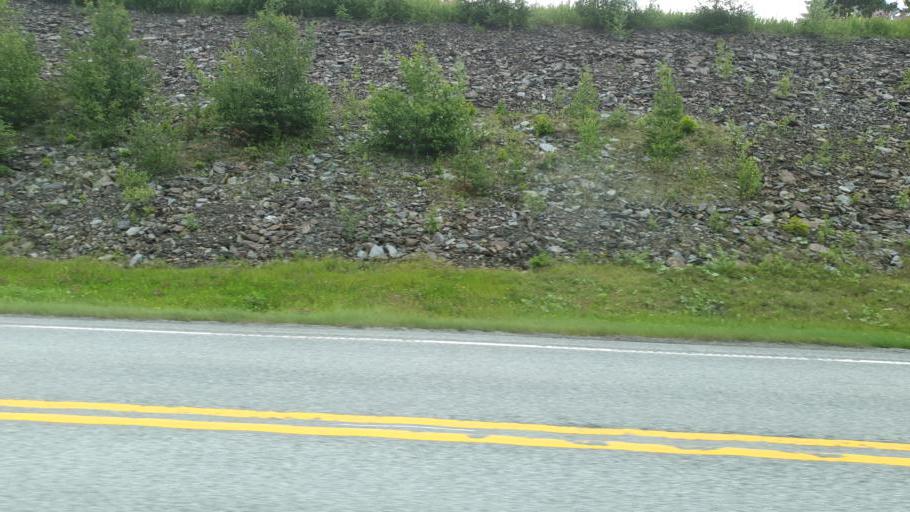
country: NO
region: Sor-Trondelag
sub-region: Rennebu
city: Berkak
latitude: 62.9253
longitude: 10.1524
